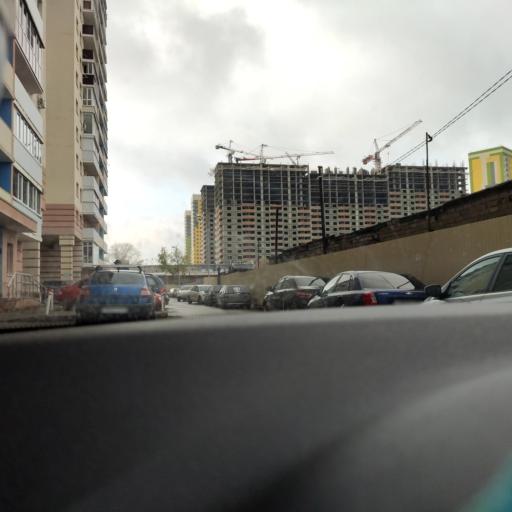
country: RU
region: Samara
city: Samara
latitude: 53.2046
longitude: 50.1813
